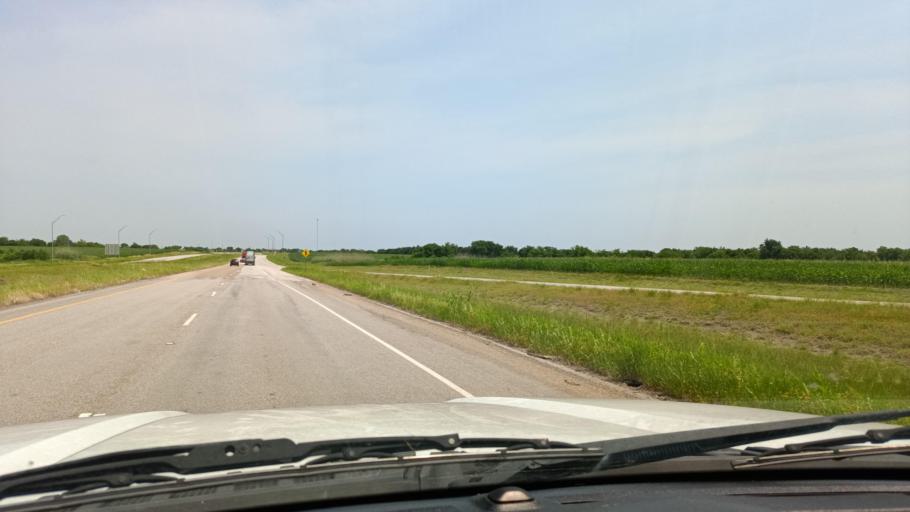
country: US
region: Texas
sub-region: Bell County
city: Little River-Academy
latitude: 31.0125
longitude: -97.3033
